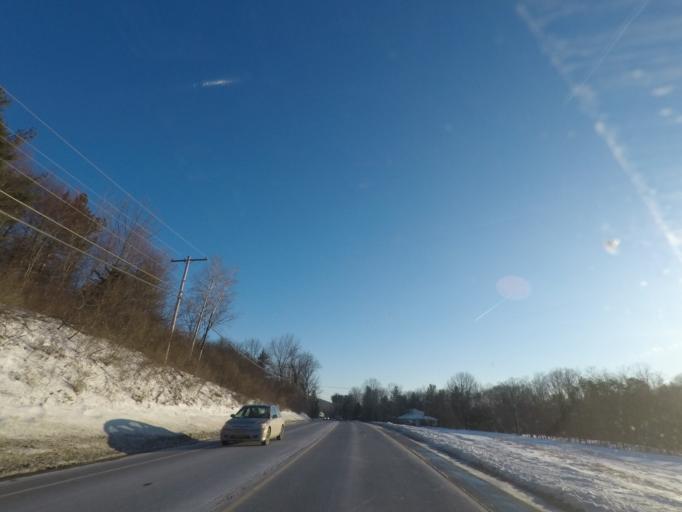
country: US
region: New York
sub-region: Saratoga County
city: Waterford
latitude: 42.8094
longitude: -73.6343
